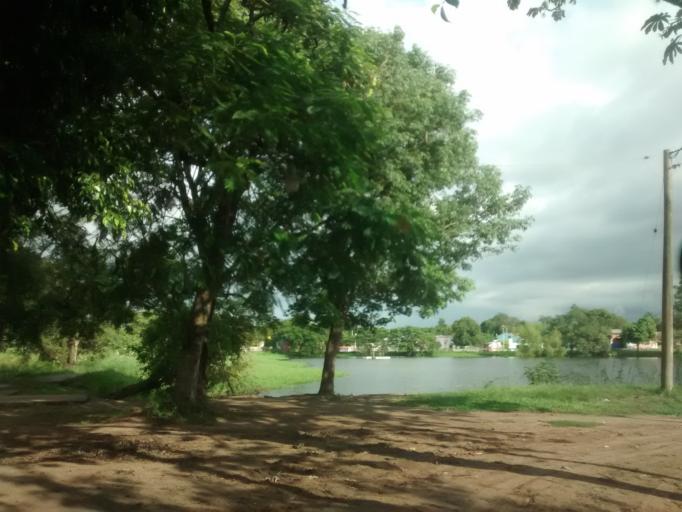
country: AR
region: Chaco
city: Puerto Tirol
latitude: -27.3758
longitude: -59.0887
